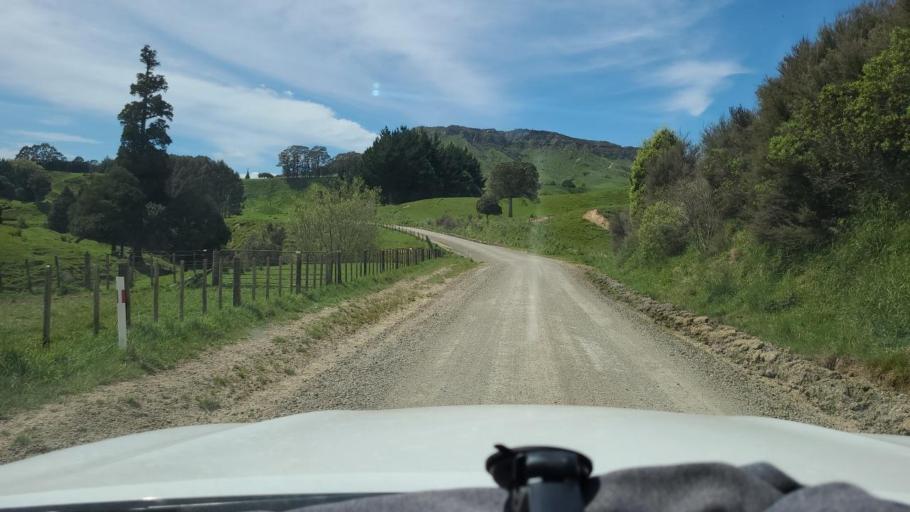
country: NZ
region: Hawke's Bay
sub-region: Wairoa District
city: Wairoa
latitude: -38.5487
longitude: 177.4757
